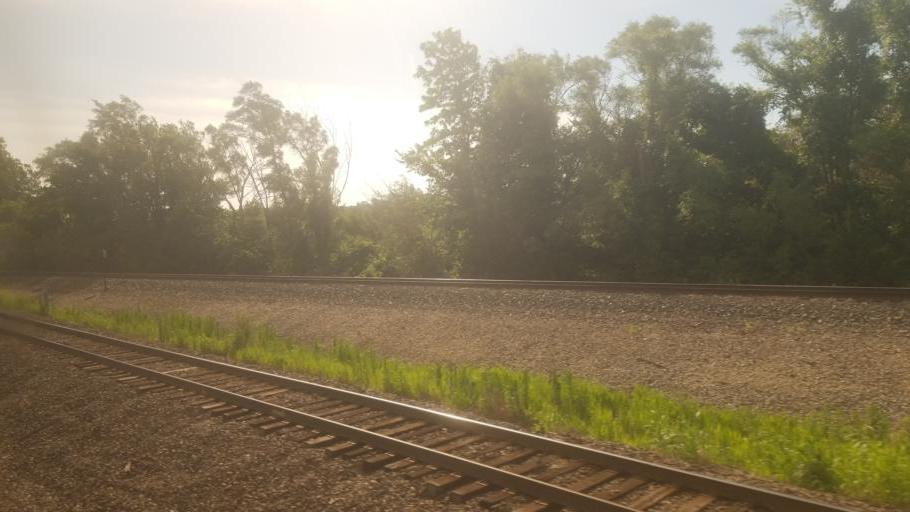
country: US
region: Kansas
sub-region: Johnson County
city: Shawnee
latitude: 39.0546
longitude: -94.7636
